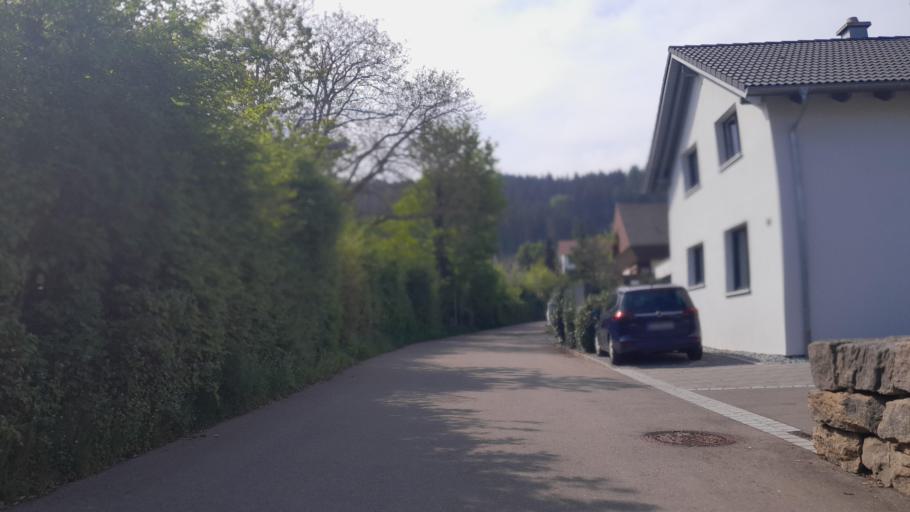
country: DE
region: Baden-Wuerttemberg
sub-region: Regierungsbezirk Stuttgart
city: Donzdorf
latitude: 48.6828
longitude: 9.8089
